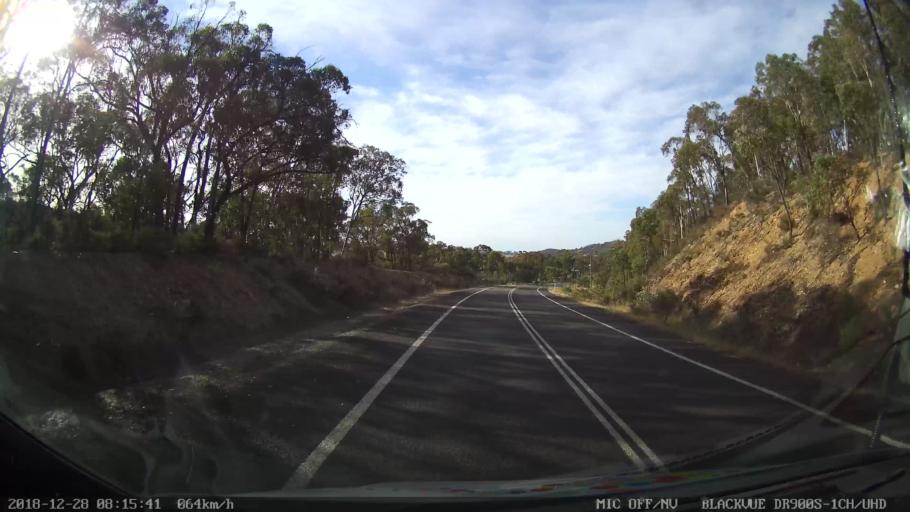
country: AU
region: New South Wales
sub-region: Blayney
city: Blayney
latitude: -33.8250
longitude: 149.3295
